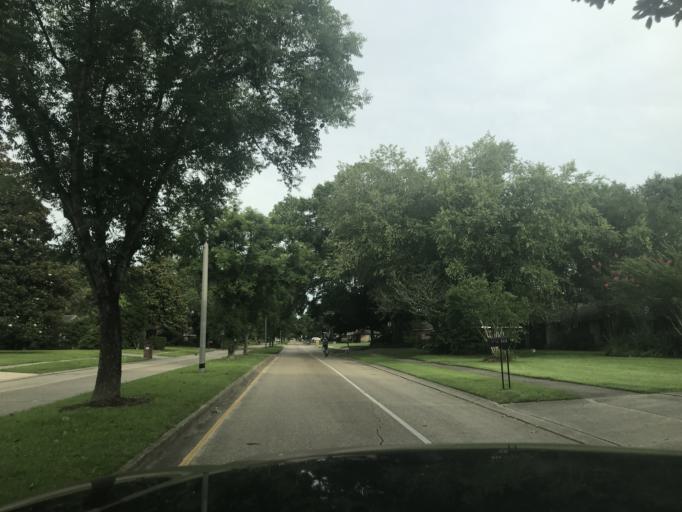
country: US
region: Louisiana
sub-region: Lafayette Parish
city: Lafayette
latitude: 30.1977
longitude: -92.0490
